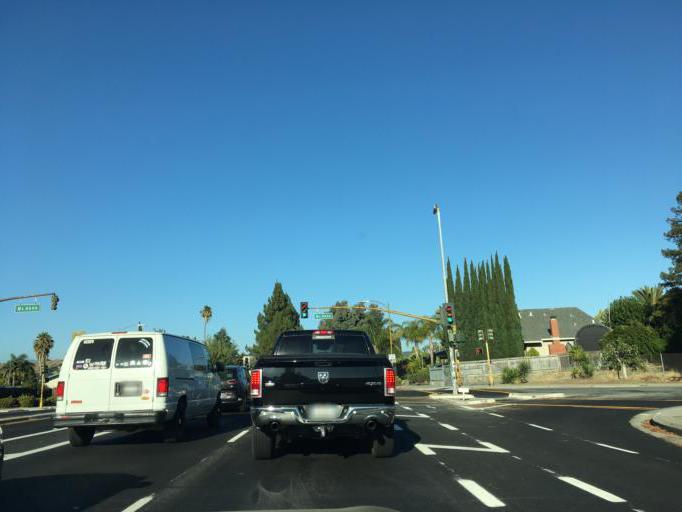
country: US
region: California
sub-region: Santa Clara County
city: Cambrian Park
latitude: 37.2219
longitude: -121.8771
